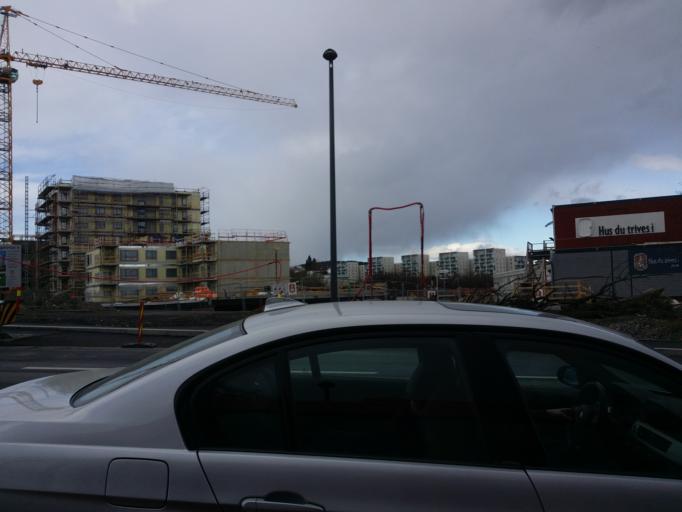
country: NO
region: Oslo
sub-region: Oslo
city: Oslo
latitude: 59.9319
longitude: 10.8003
